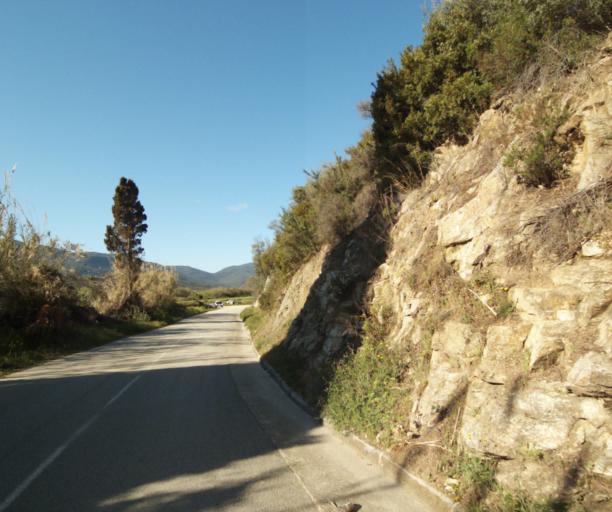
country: FR
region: Corsica
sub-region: Departement de la Corse-du-Sud
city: Propriano
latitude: 41.6655
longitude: 8.8933
